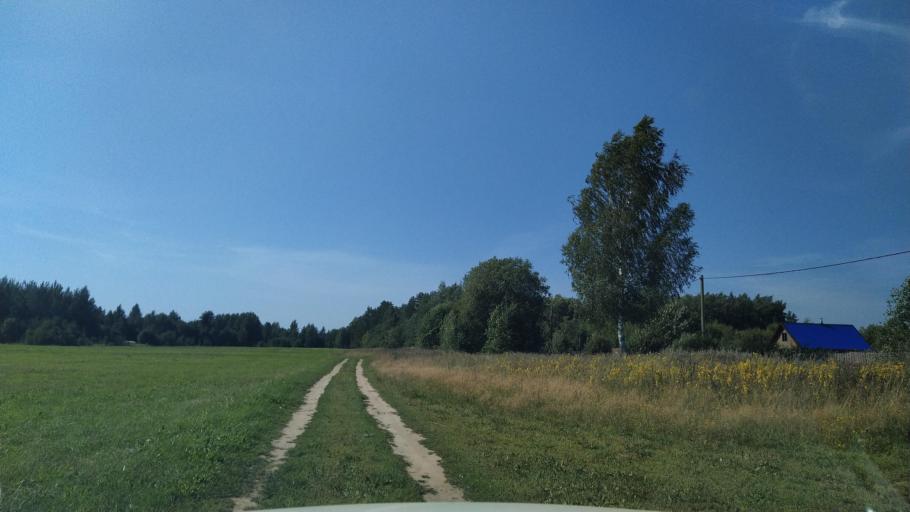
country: RU
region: Leningrad
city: Druzhnaya Gorka
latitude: 59.2687
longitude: 30.0566
